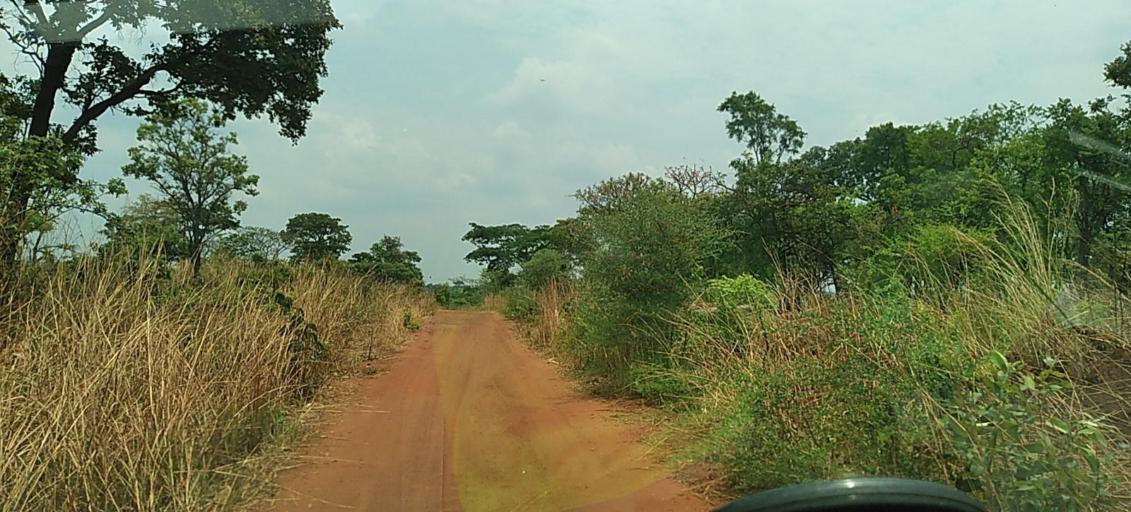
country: ZM
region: North-Western
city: Kansanshi
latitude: -12.0485
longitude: 26.3708
